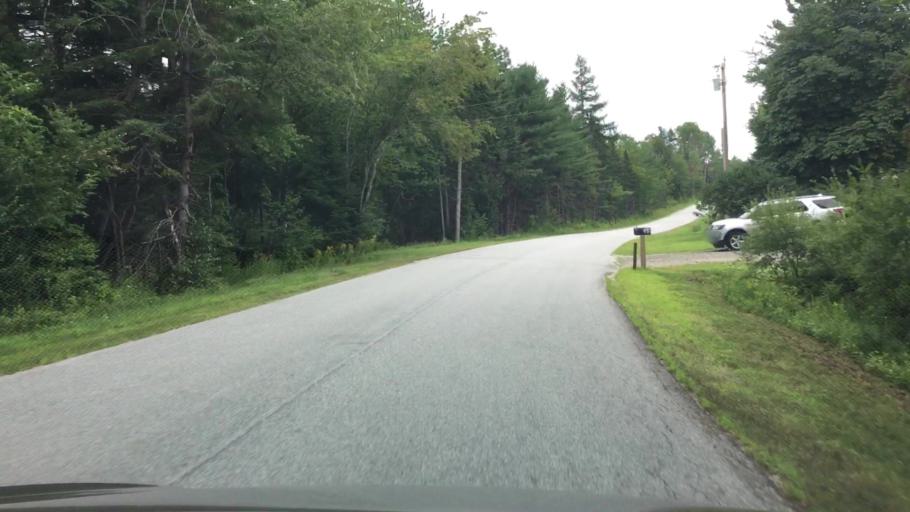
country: US
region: Maine
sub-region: Waldo County
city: Stockton Springs
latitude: 44.5292
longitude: -68.8317
